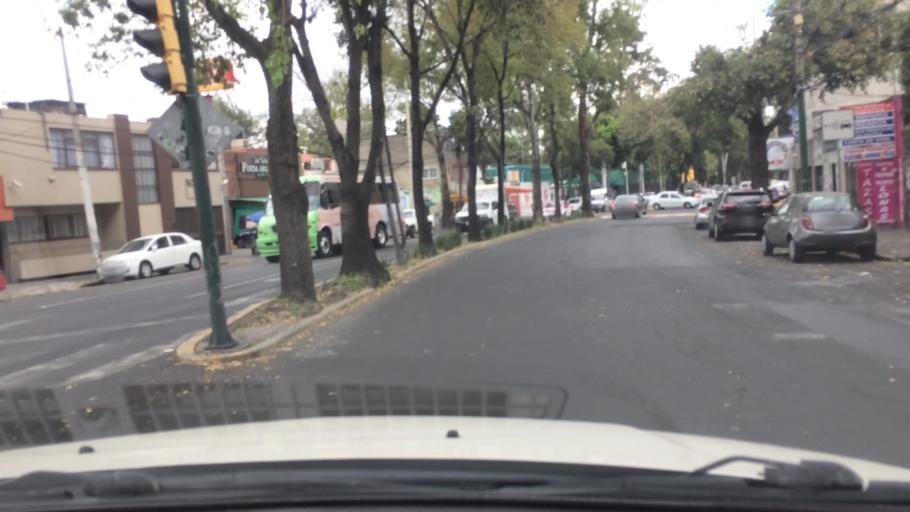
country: MX
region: Mexico City
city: Tlalpan
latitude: 19.2951
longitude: -99.1756
